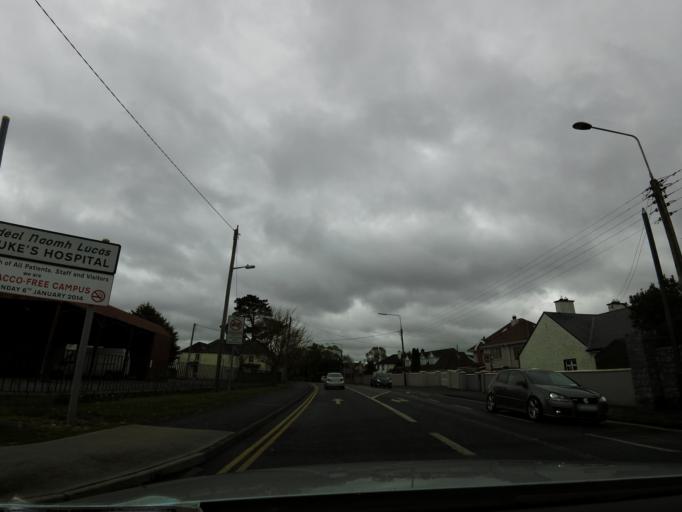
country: IE
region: Leinster
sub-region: Kilkenny
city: Kilkenny
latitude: 52.6671
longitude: -7.2656
